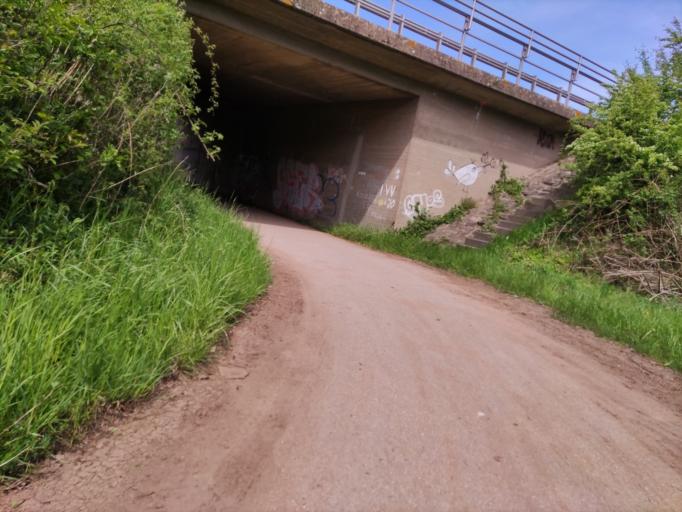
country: DE
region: Saarland
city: Saarwellingen
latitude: 49.3460
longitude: 6.7816
